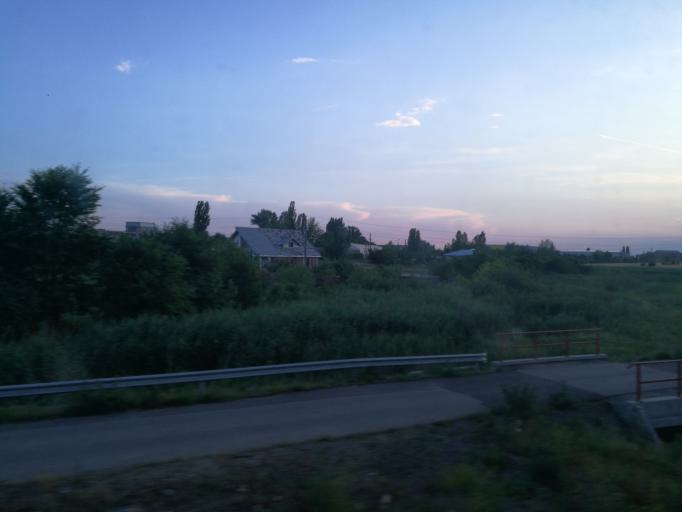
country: RO
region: Ilfov
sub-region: Comuna Chitila
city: Chitila
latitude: 44.5057
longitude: 25.9780
